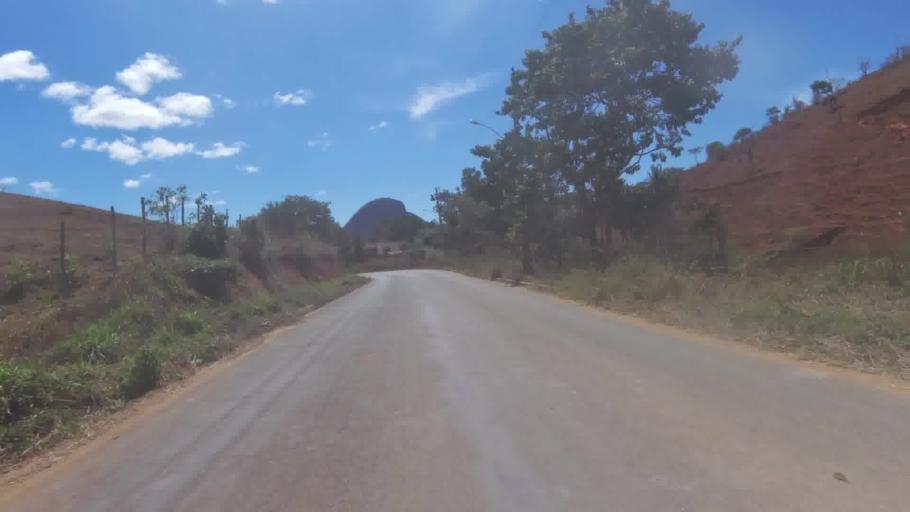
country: BR
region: Espirito Santo
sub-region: Cachoeiro De Itapemirim
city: Cachoeiro de Itapemirim
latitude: -20.9337
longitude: -41.2150
